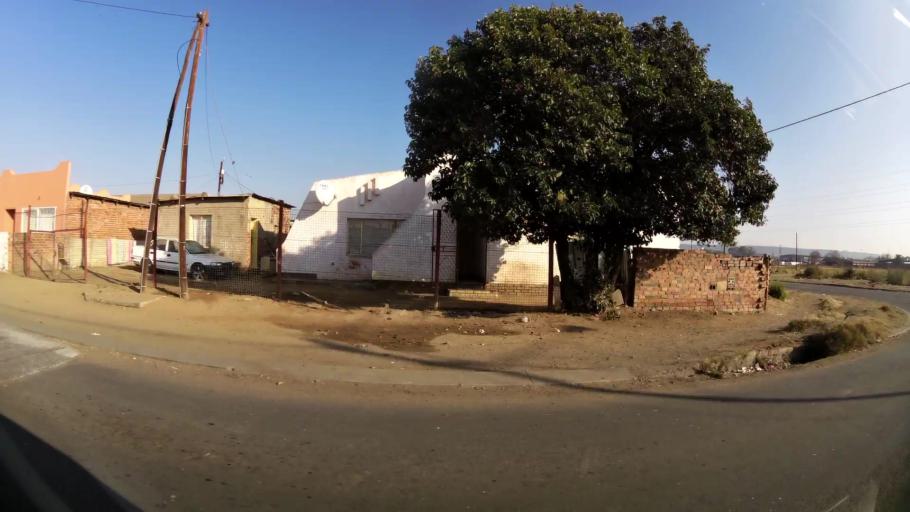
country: ZA
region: Orange Free State
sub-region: Mangaung Metropolitan Municipality
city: Bloemfontein
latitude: -29.1327
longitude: 26.2532
